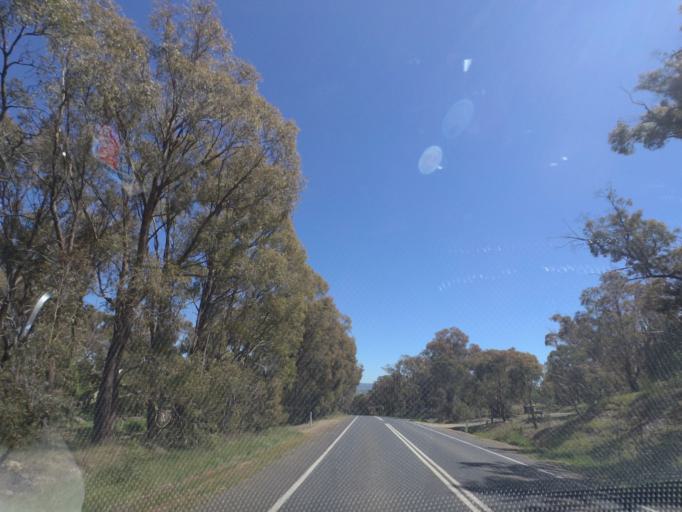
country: AU
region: Victoria
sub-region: Hume
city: Sunbury
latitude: -37.2932
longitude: 144.7959
